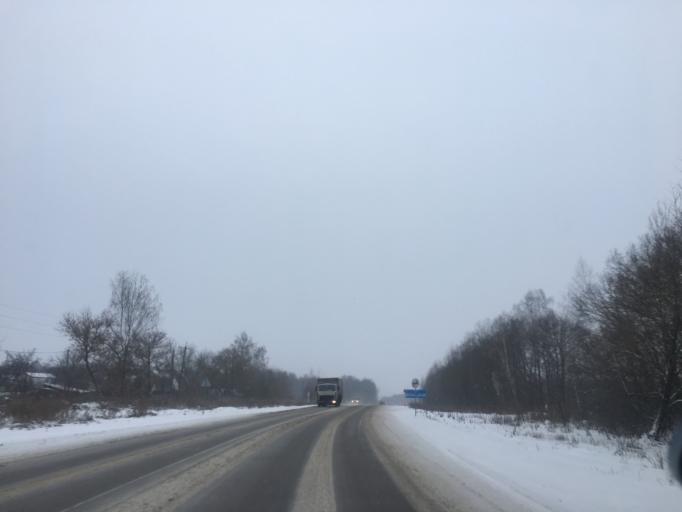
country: RU
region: Tula
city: Kosaya Gora
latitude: 54.1775
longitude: 37.5036
